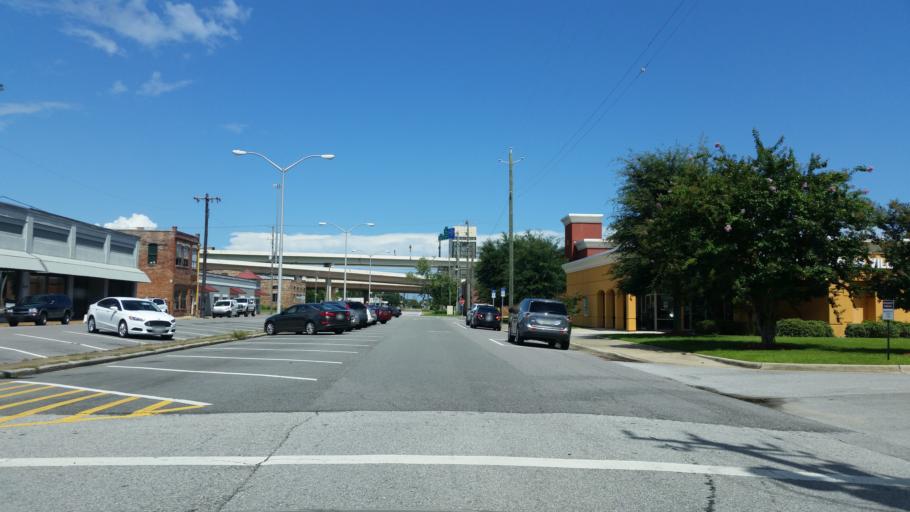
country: US
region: Florida
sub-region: Escambia County
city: Pensacola
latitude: 30.4169
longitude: -87.2149
